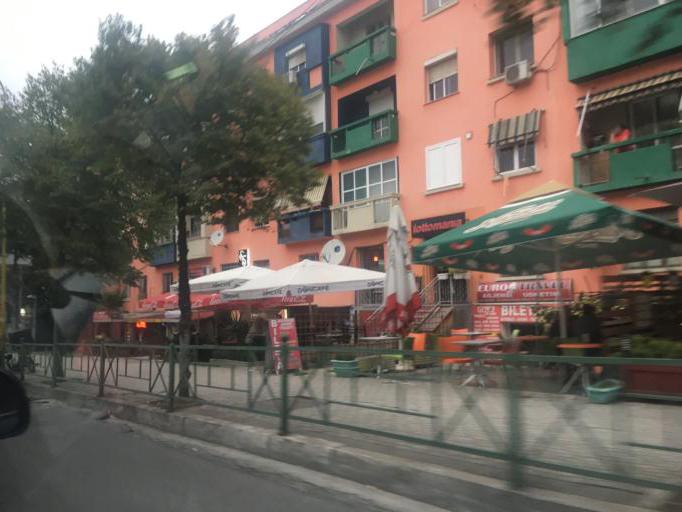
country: AL
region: Tirane
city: Tirana
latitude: 41.3326
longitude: 19.8058
